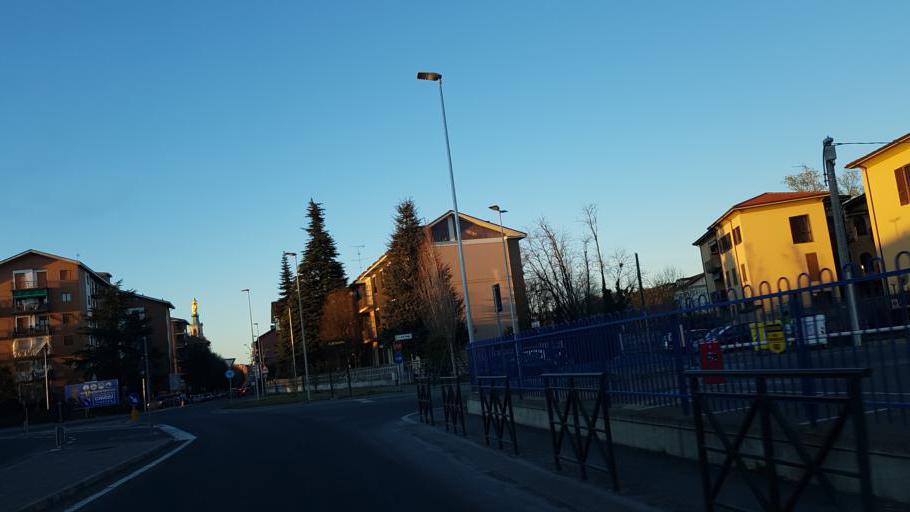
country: IT
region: Piedmont
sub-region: Provincia di Alessandria
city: Tortona
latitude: 44.8831
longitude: 8.8588
